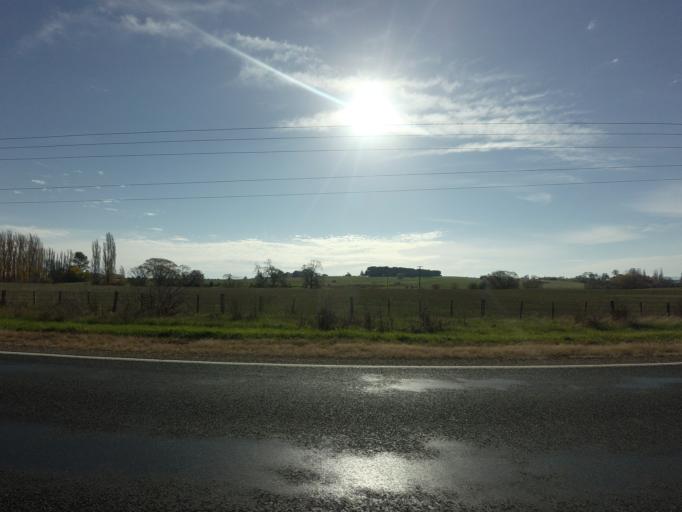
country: AU
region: Tasmania
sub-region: Meander Valley
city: Westbury
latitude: -41.5291
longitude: 146.9254
